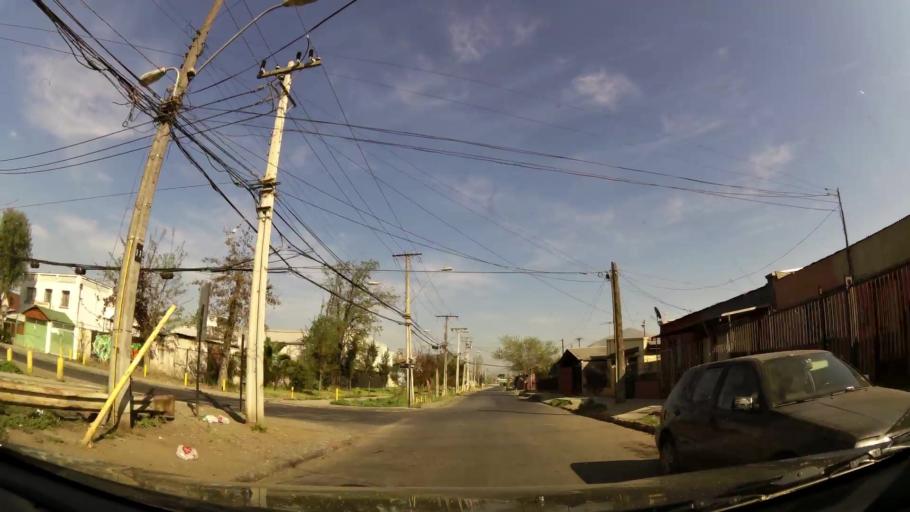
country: CL
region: Santiago Metropolitan
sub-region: Provincia de Santiago
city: Santiago
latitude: -33.4071
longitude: -70.6769
